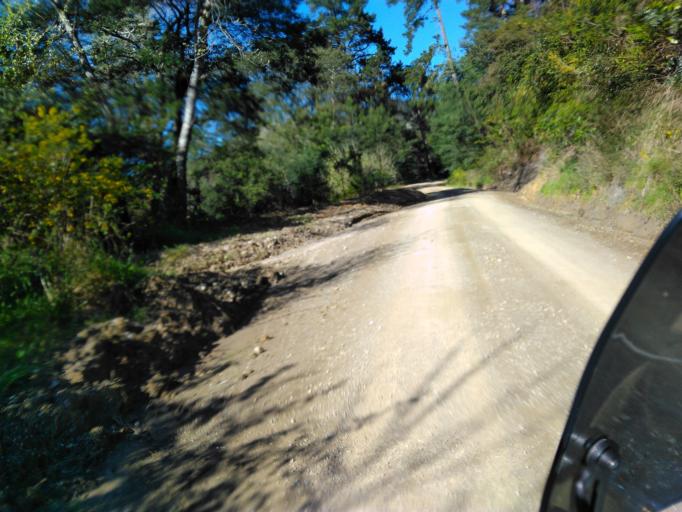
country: NZ
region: Gisborne
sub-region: Gisborne District
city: Gisborne
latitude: -38.4118
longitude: 177.6906
